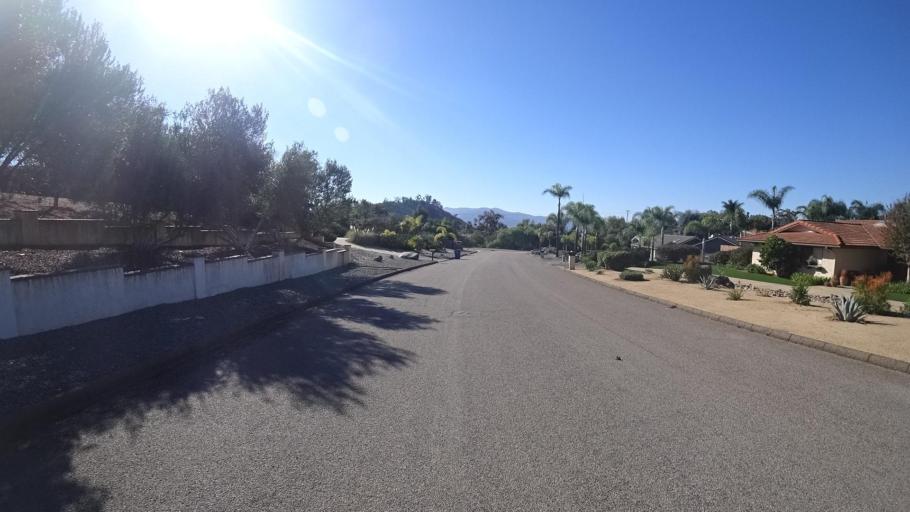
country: US
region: California
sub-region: San Diego County
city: Jamul
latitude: 32.7234
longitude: -116.8589
